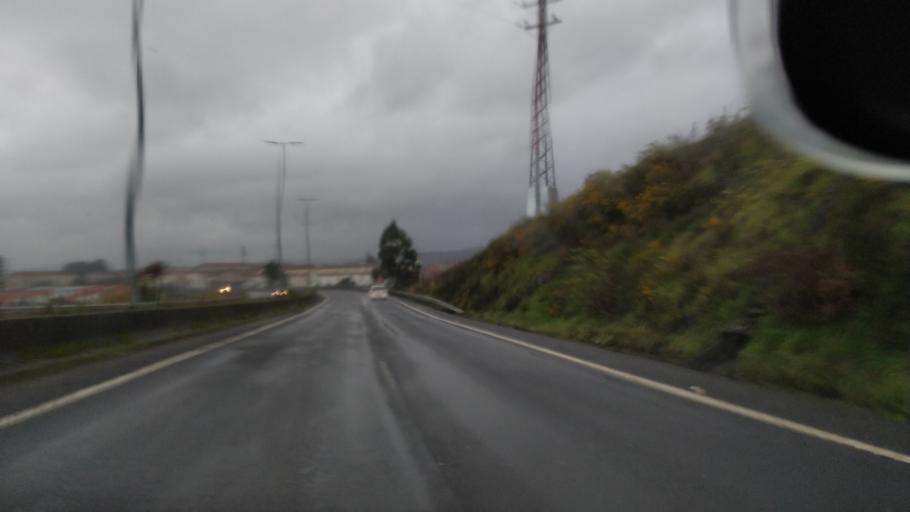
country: ES
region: Galicia
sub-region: Provincia da Coruna
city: Santiago de Compostela
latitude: 42.8607
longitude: -8.5470
